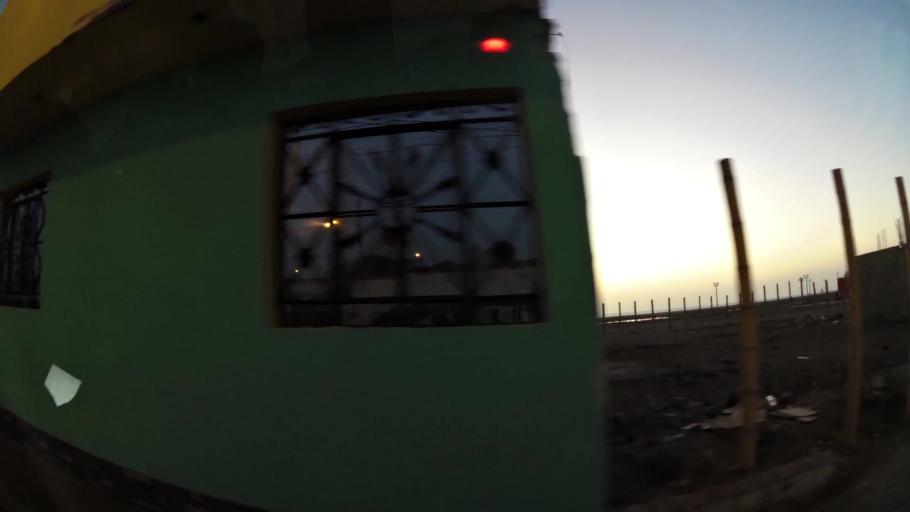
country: PE
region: Ica
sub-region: Provincia de Pisco
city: Pisco
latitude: -13.7098
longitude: -76.2182
